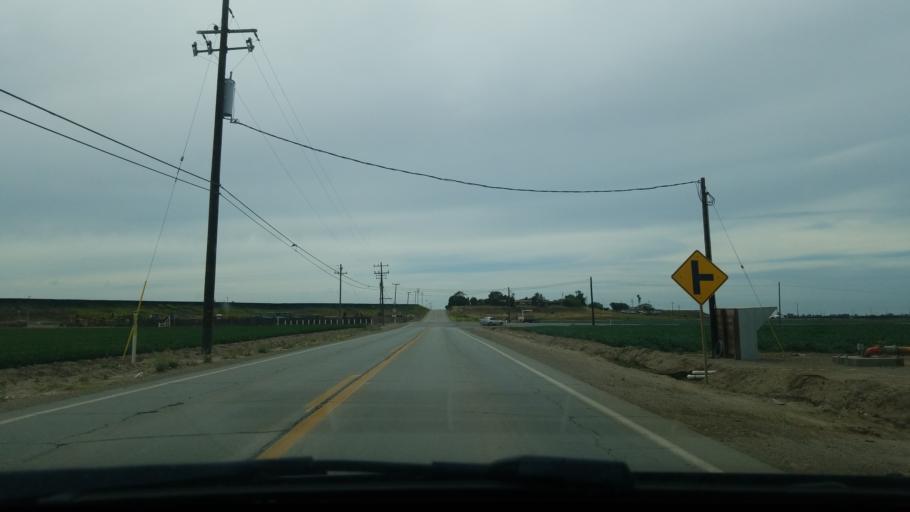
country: US
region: California
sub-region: Santa Barbara County
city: Santa Maria
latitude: 34.9234
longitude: -120.3726
